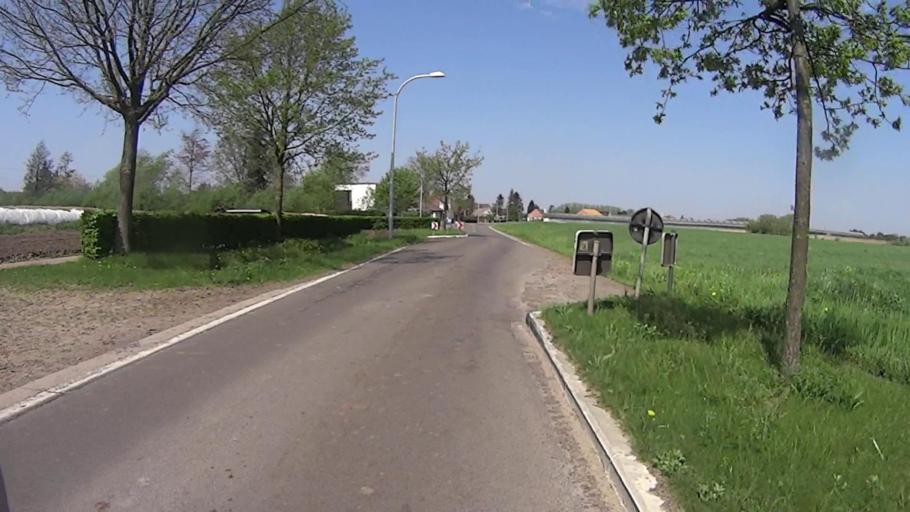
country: BE
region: Flanders
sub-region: Provincie Antwerpen
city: Sint-Amands
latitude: 51.0485
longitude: 4.2323
